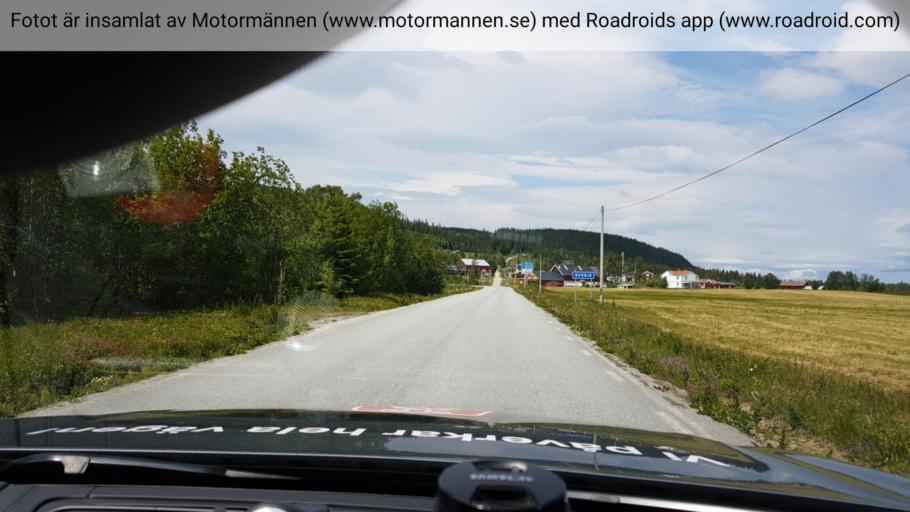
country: SE
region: Jaemtland
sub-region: Bergs Kommun
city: Hoverberg
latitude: 62.9149
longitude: 14.3213
